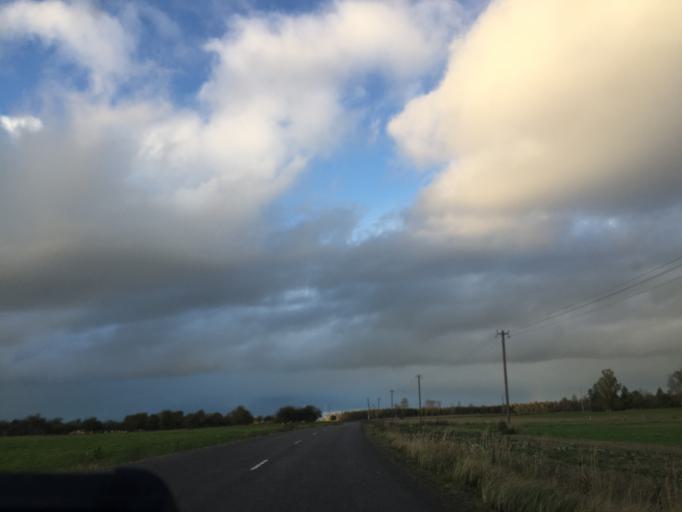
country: LV
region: Talsu Rajons
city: Sabile
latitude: 56.9186
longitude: 22.3962
